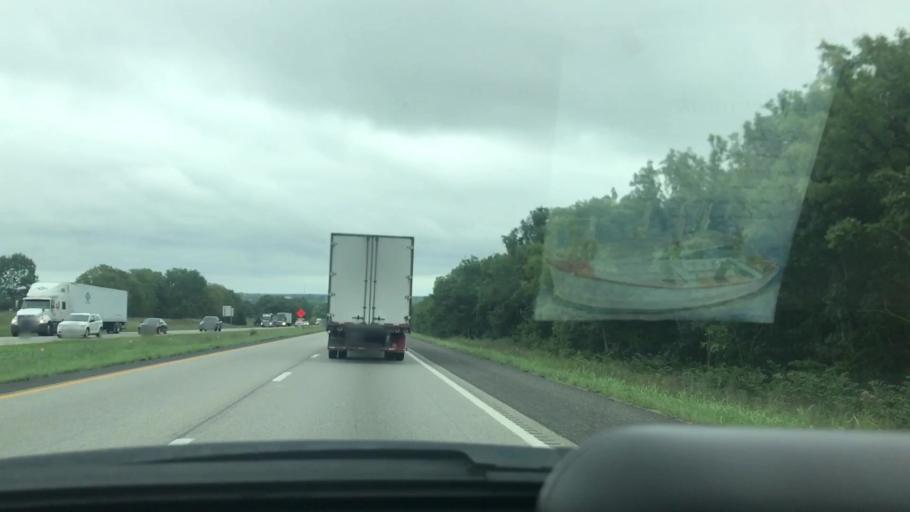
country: US
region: Missouri
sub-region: Greene County
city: Republic
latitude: 37.1858
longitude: -93.5505
